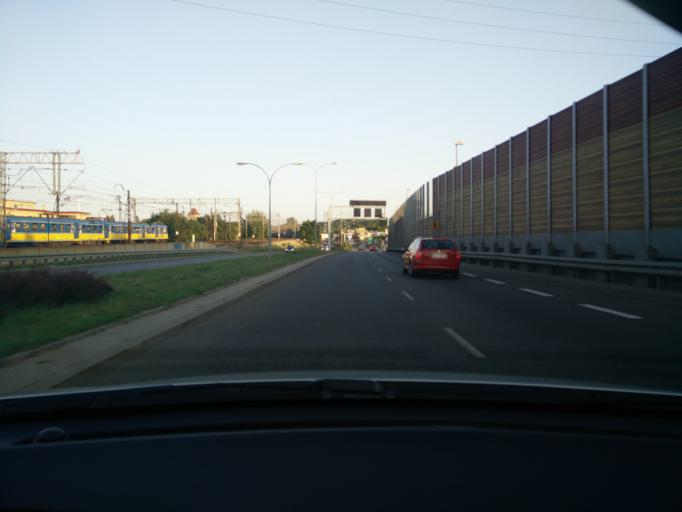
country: PL
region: Pomeranian Voivodeship
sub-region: Gdynia
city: Gdynia
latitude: 54.4892
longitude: 18.5387
